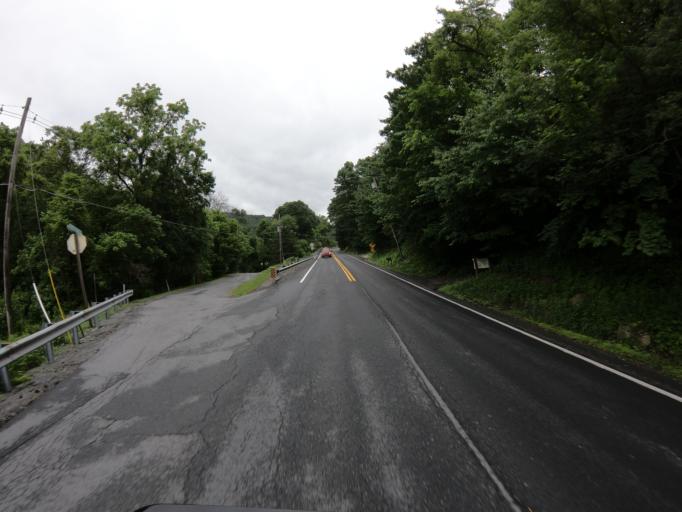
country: US
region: Maryland
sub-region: Washington County
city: Boonsboro
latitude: 39.4873
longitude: -77.6296
